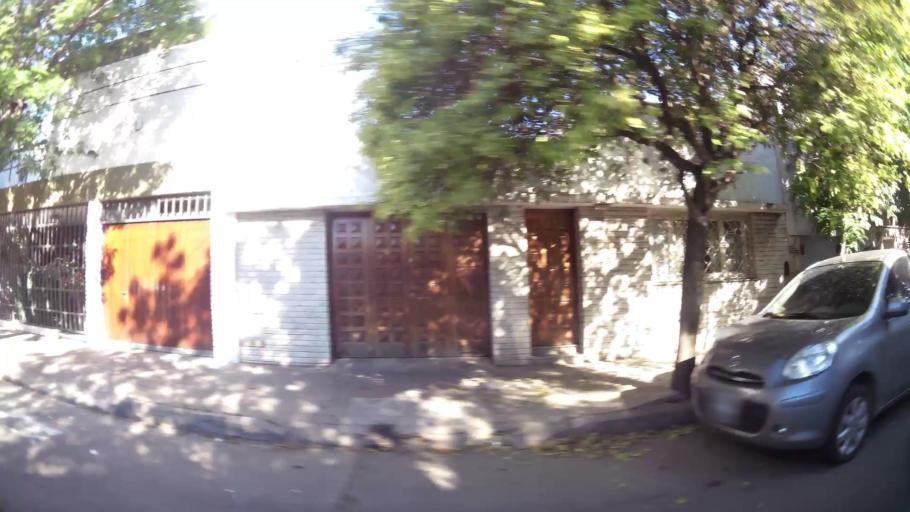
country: AR
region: Cordoba
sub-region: Departamento de Capital
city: Cordoba
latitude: -31.3934
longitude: -64.1722
